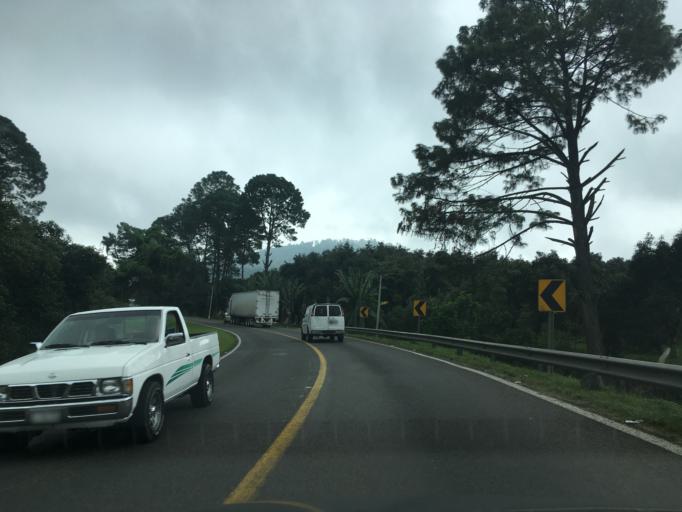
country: MX
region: Michoacan
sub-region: Uruapan
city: Toreo Bajo (El Toreo Bajo)
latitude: 19.4535
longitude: -101.9929
